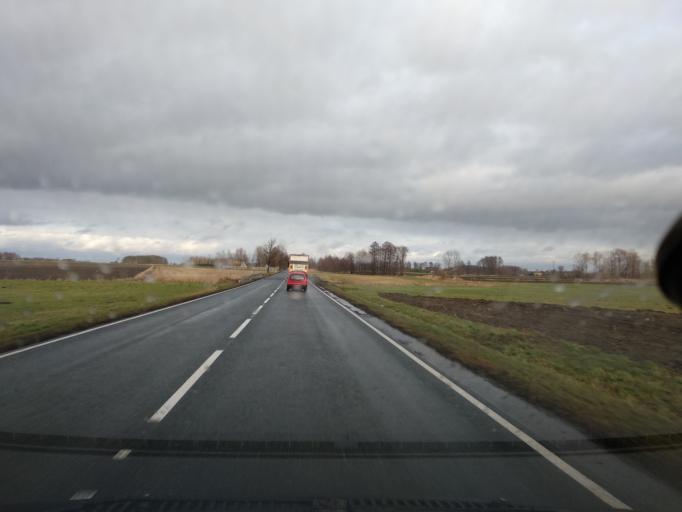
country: PL
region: Greater Poland Voivodeship
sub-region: Powiat koninski
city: Rychwal
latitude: 52.1290
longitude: 18.1787
